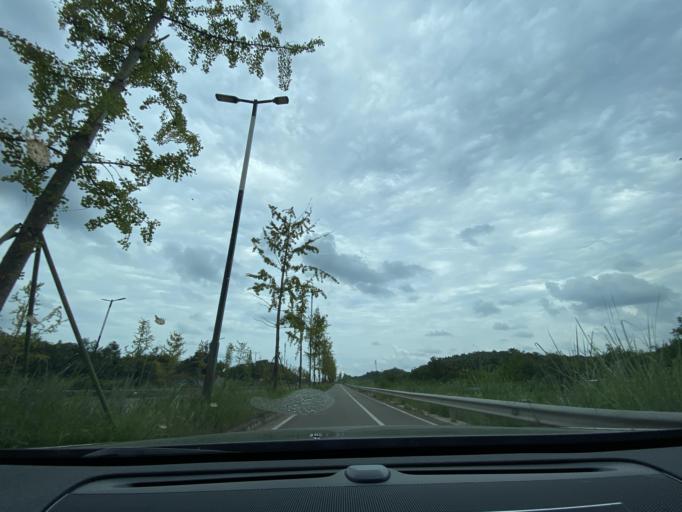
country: CN
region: Sichuan
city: Jiancheng
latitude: 30.4894
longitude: 104.4721
